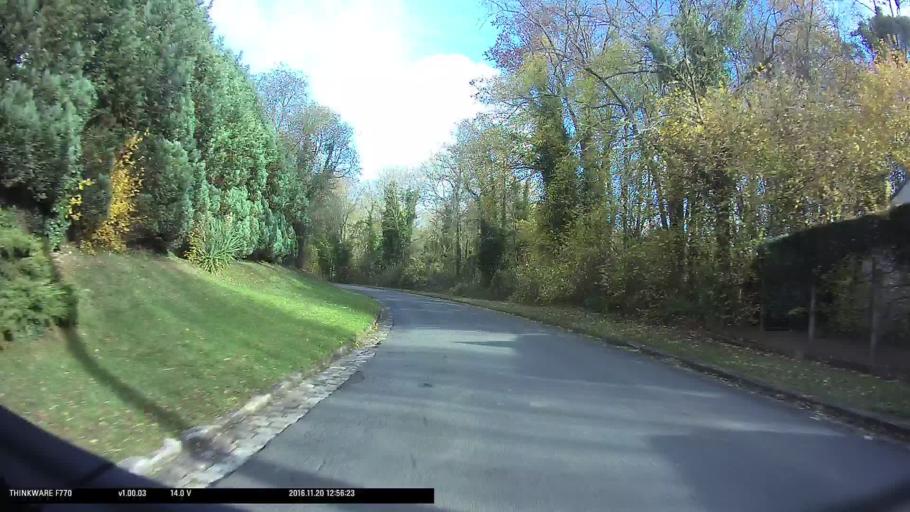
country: FR
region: Ile-de-France
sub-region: Departement du Val-d'Oise
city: Sagy
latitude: 49.0582
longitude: 1.9583
